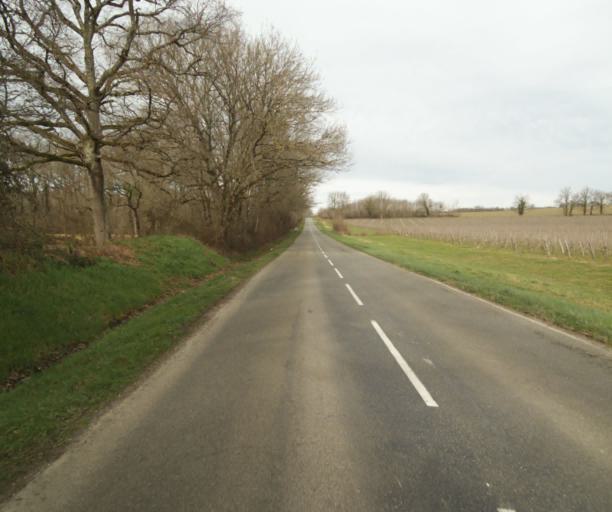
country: FR
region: Aquitaine
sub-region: Departement des Landes
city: Gabarret
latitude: 43.9559
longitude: 0.0082
